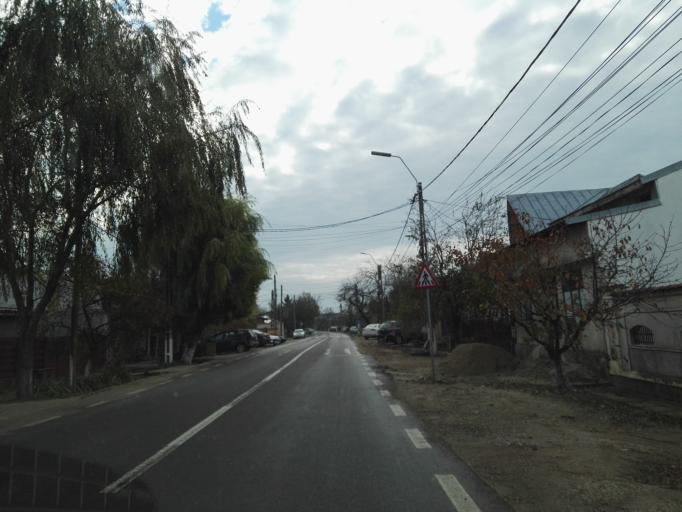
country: RO
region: Ilfov
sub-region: Comuna Magurele
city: Alunisu
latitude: 44.3395
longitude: 26.0545
